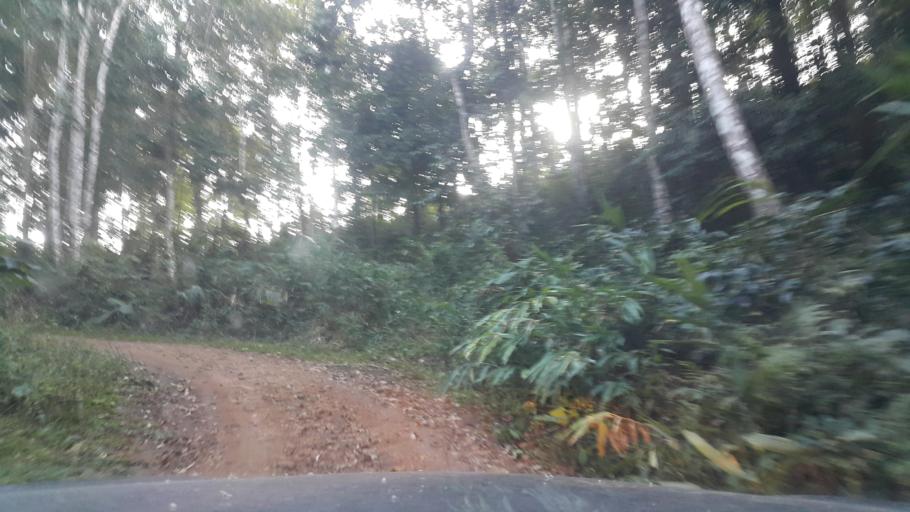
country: TH
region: Chiang Mai
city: Samoeng
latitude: 19.0194
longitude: 98.6508
